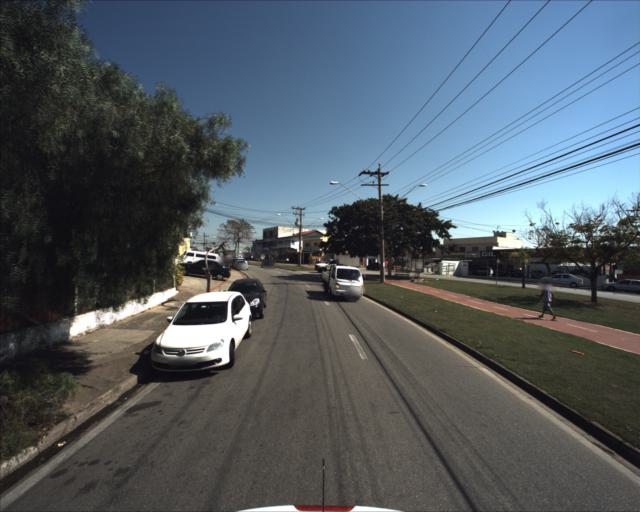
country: BR
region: Sao Paulo
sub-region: Sorocaba
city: Sorocaba
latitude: -23.5033
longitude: -47.5157
